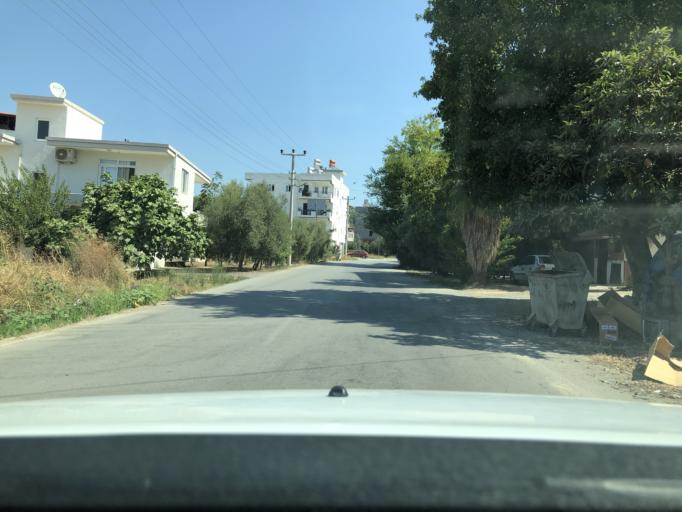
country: TR
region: Antalya
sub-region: Manavgat
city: Manavgat
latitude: 36.8094
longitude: 31.4822
